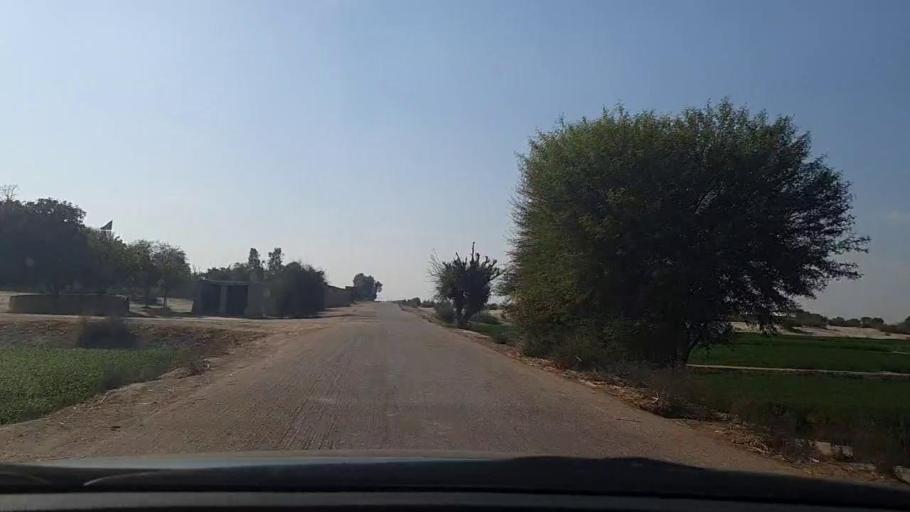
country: PK
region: Sindh
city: Daulatpur
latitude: 26.3213
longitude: 68.0206
